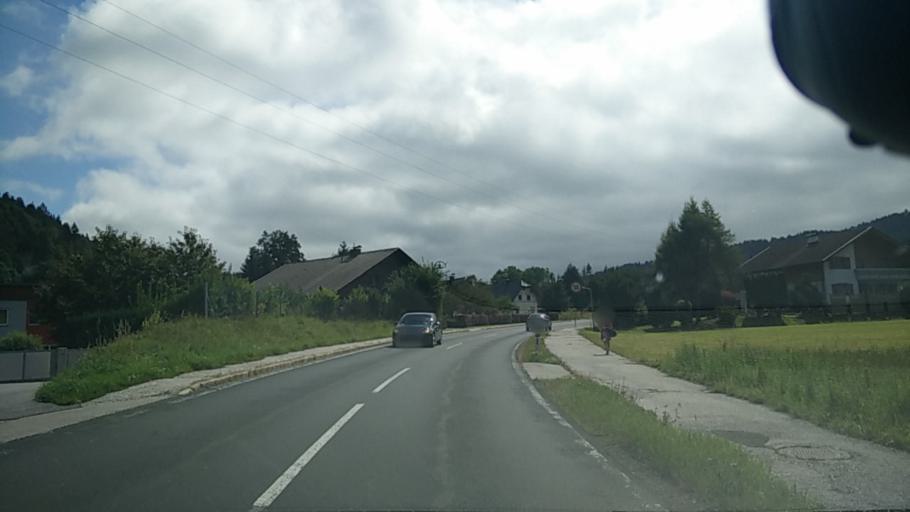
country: AT
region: Carinthia
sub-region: Politischer Bezirk Villach Land
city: Finkenstein am Faaker See
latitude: 46.5595
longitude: 13.9162
